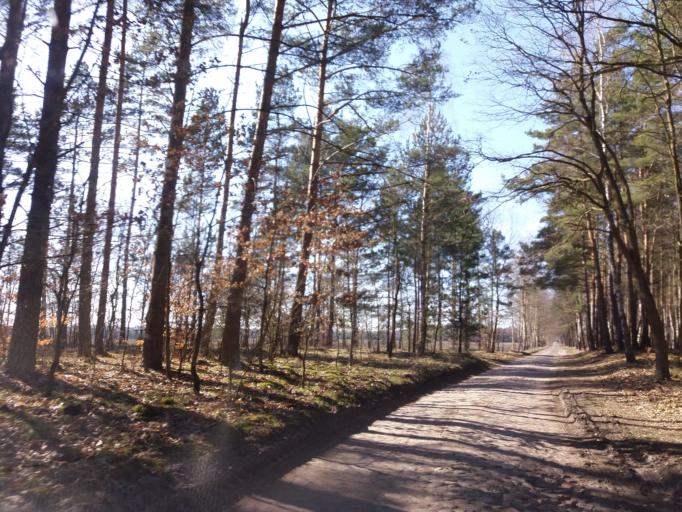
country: PL
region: Lubusz
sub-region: Powiat strzelecko-drezdenecki
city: Dobiegniew
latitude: 53.0872
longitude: 15.8086
